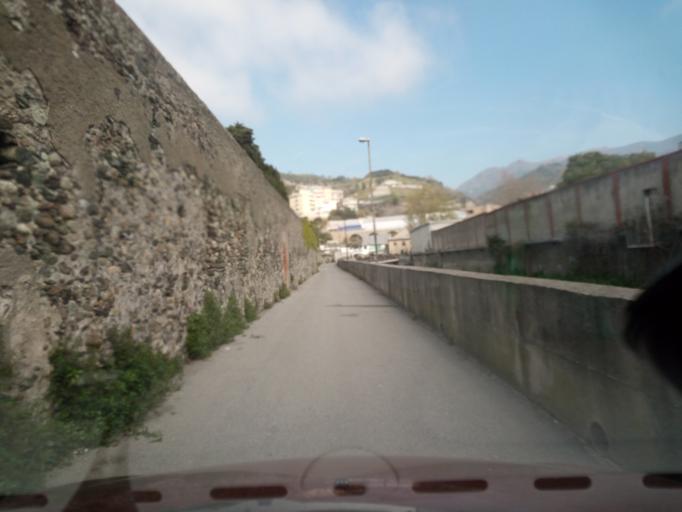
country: IT
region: Liguria
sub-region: Provincia di Genova
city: Mele
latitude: 44.4275
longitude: 8.7764
